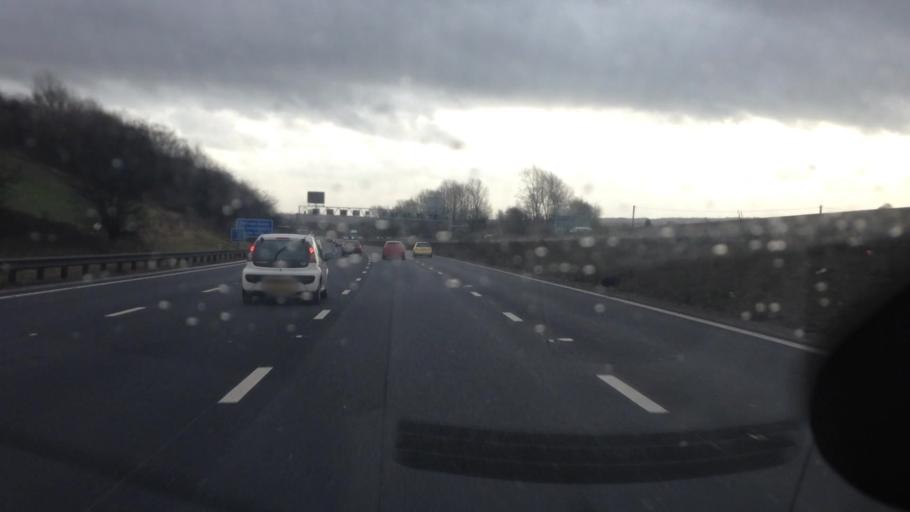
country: GB
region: England
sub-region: City and Borough of Wakefield
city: Horbury
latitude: 53.6731
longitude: -1.5500
